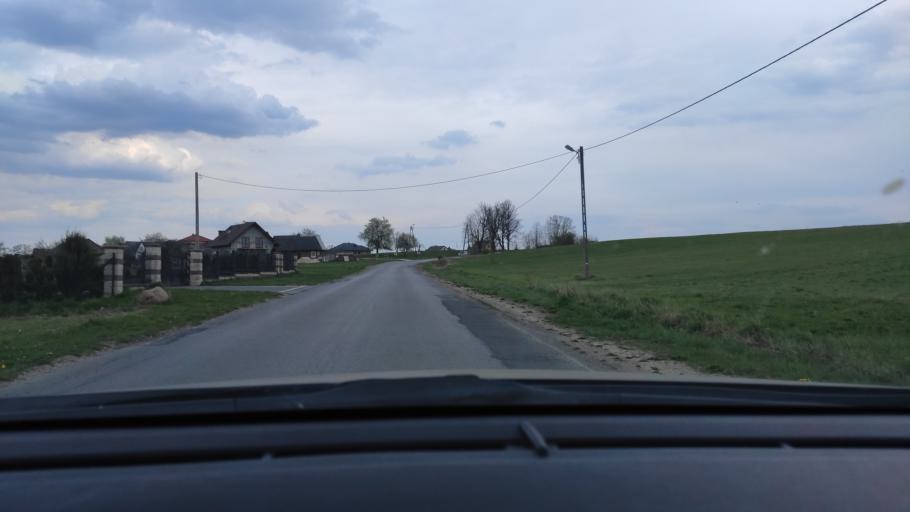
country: PL
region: Masovian Voivodeship
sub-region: Powiat kozienicki
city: Ryczywol
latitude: 51.5953
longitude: 21.3494
